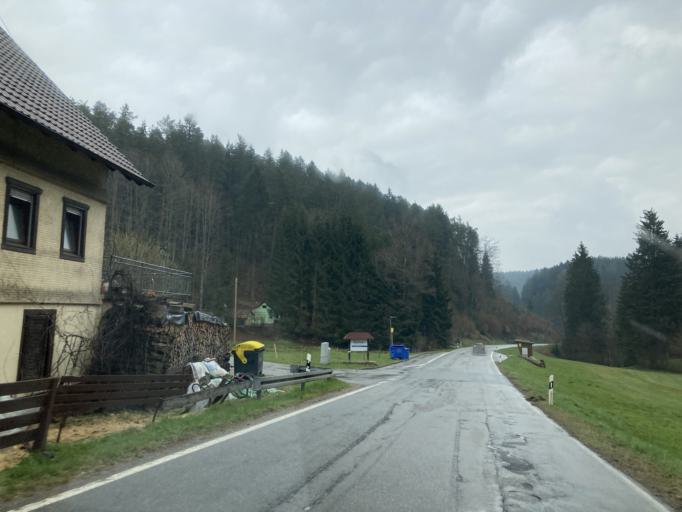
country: DE
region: Baden-Wuerttemberg
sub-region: Freiburg Region
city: Lauterbach/Schwarzwald
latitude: 48.2286
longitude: 8.3182
